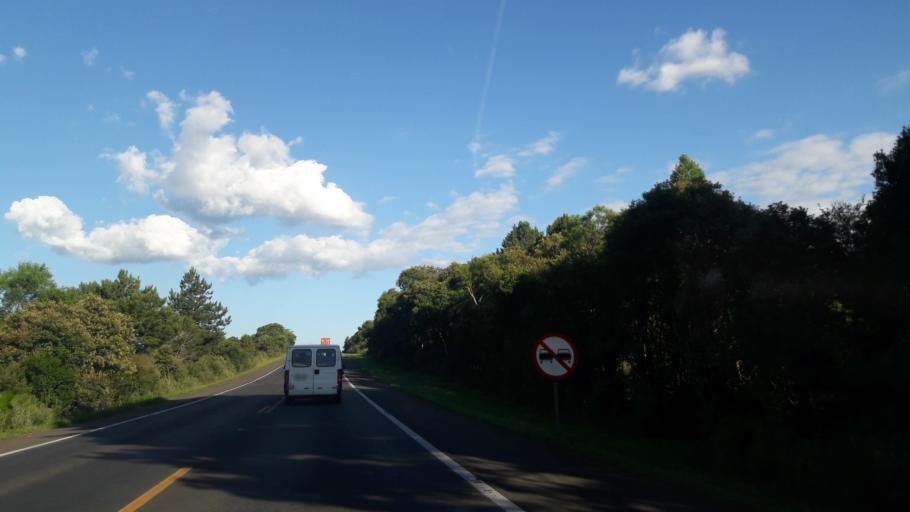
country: BR
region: Parana
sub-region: Guarapuava
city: Guarapuava
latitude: -25.3683
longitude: -51.3321
